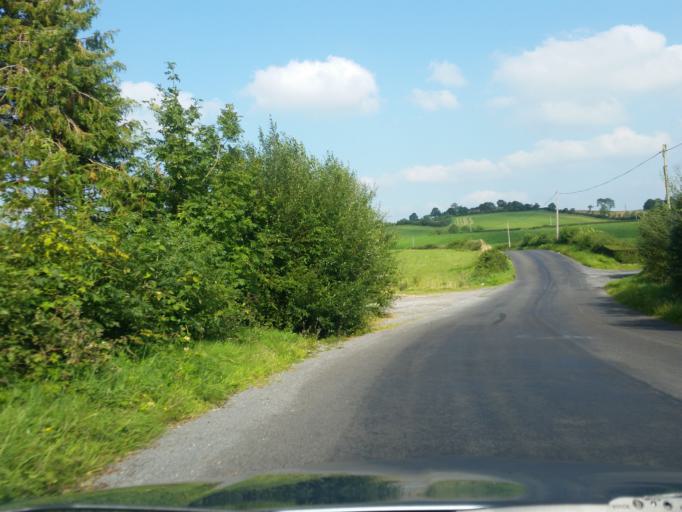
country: GB
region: Northern Ireland
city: Ballinamallard
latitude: 54.3703
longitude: -7.5991
